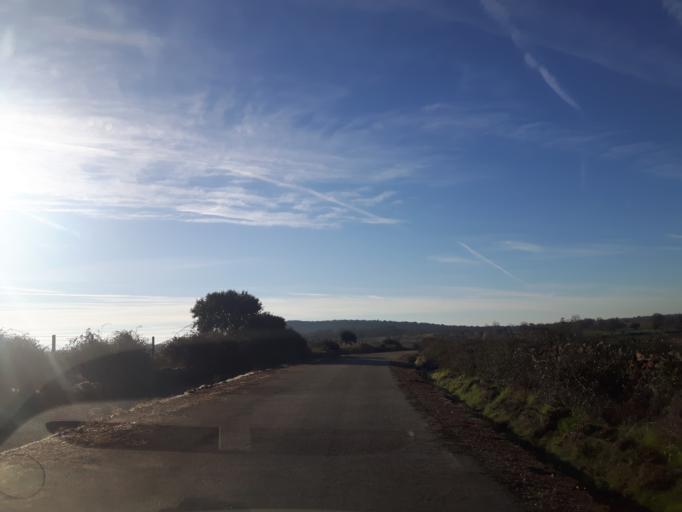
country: ES
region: Castille and Leon
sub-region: Provincia de Salamanca
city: Olmedo de Camaces
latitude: 40.9194
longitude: -6.6166
